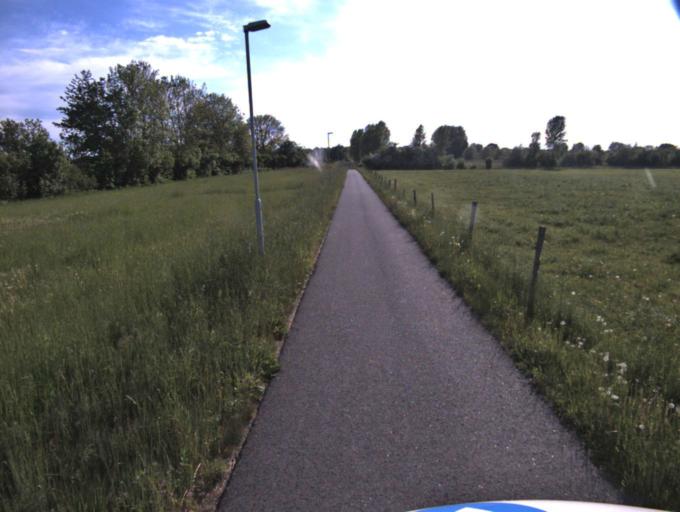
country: SE
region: Skane
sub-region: Kristianstads Kommun
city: Kristianstad
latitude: 56.0477
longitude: 14.2002
